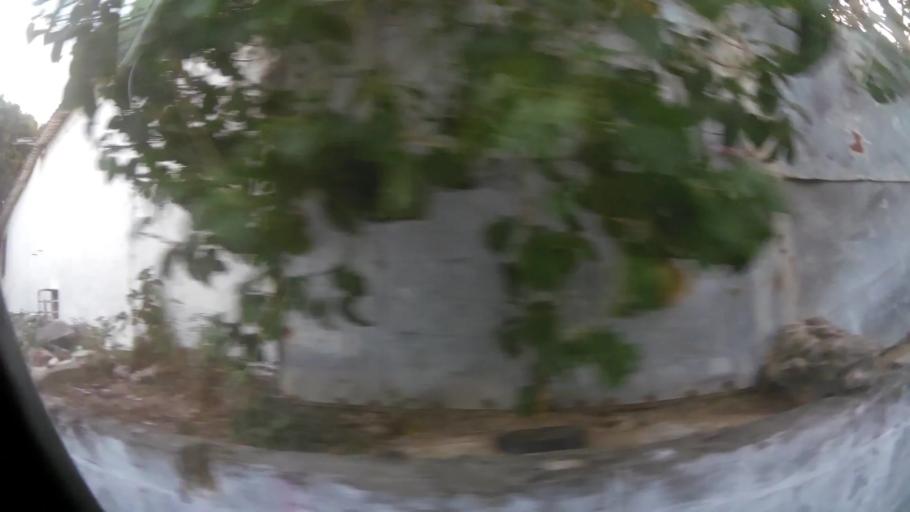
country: CO
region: Atlantico
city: Barranquilla
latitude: 10.9610
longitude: -74.8261
